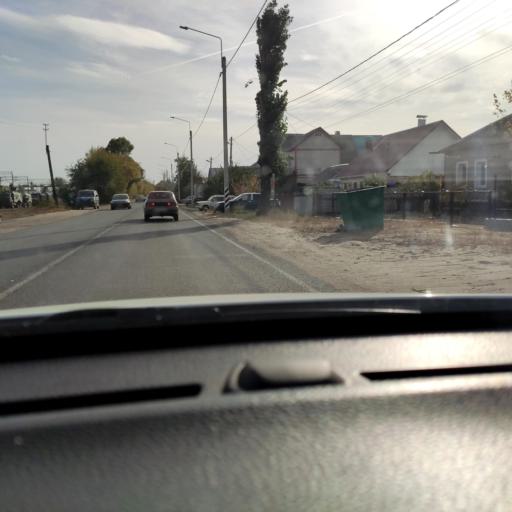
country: RU
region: Voronezj
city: Maslovka
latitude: 51.5649
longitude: 39.2455
